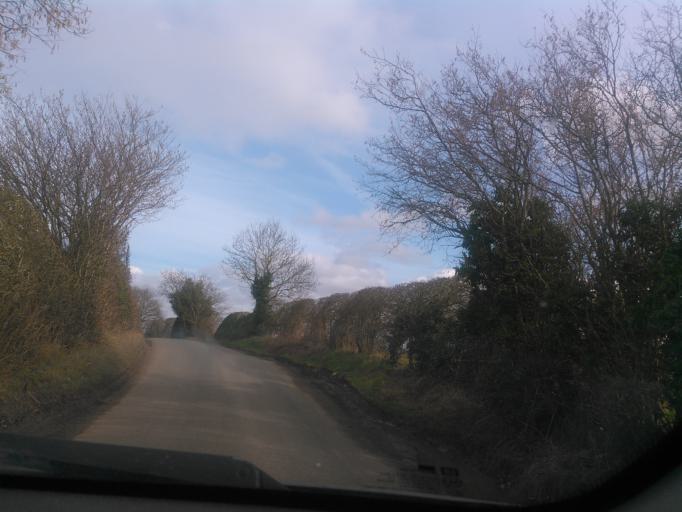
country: GB
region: England
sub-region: Shropshire
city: Clive
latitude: 52.7799
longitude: -2.7550
